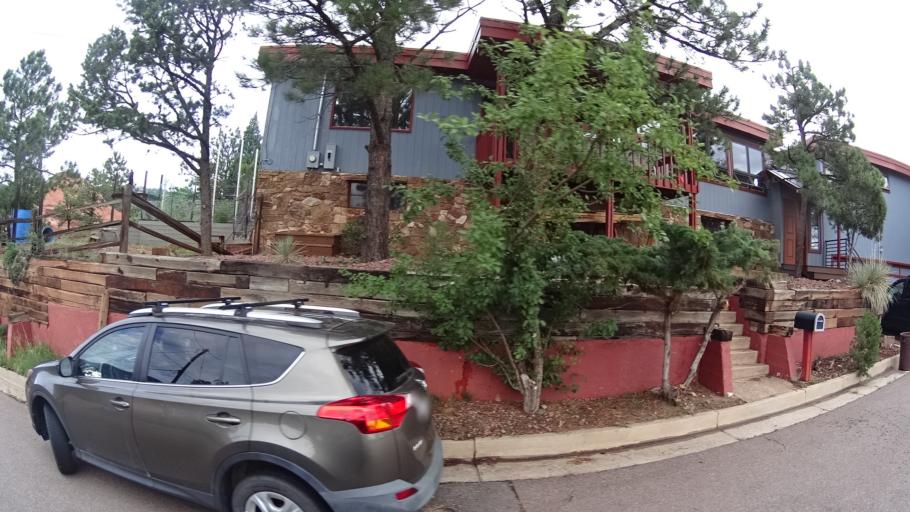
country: US
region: Colorado
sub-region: El Paso County
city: Manitou Springs
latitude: 38.8617
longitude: -104.8896
